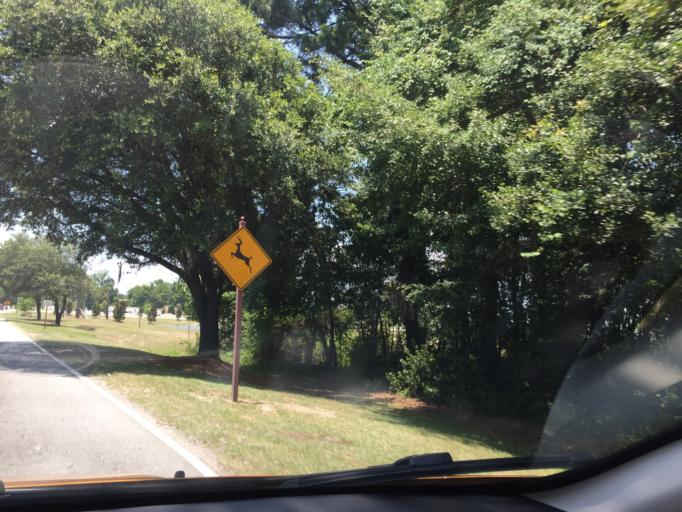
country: US
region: South Carolina
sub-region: Berkeley County
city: Hanahan
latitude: 32.8691
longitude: -80.0291
